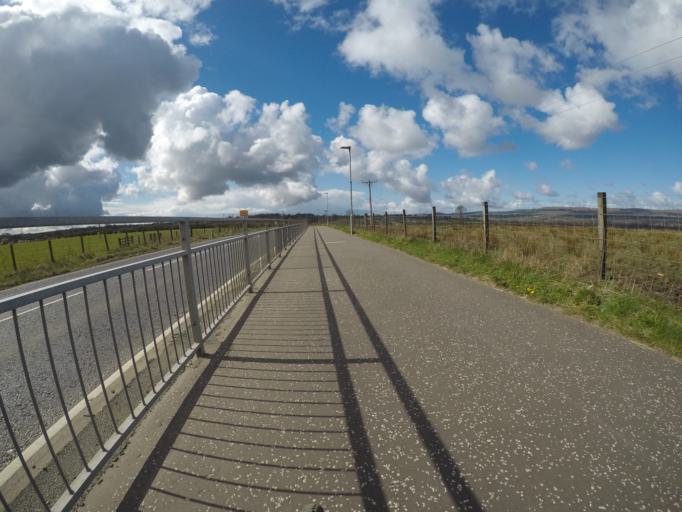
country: GB
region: Scotland
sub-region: North Ayrshire
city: Beith
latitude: 55.7410
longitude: -4.6534
